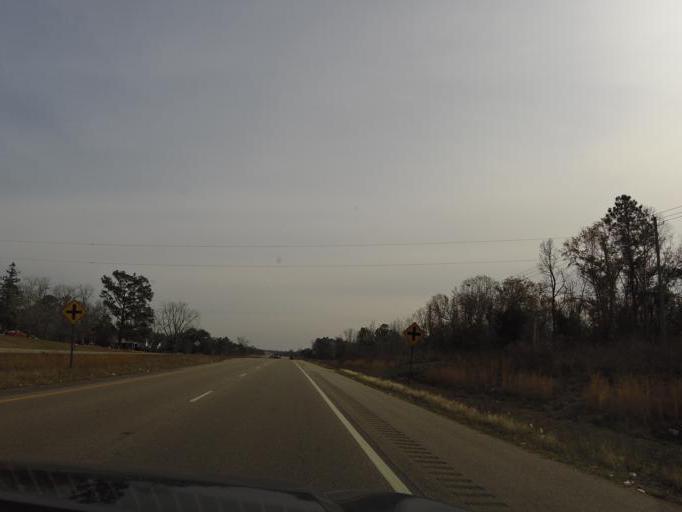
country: US
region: Alabama
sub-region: Houston County
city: Ashford
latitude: 31.1594
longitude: -85.1881
